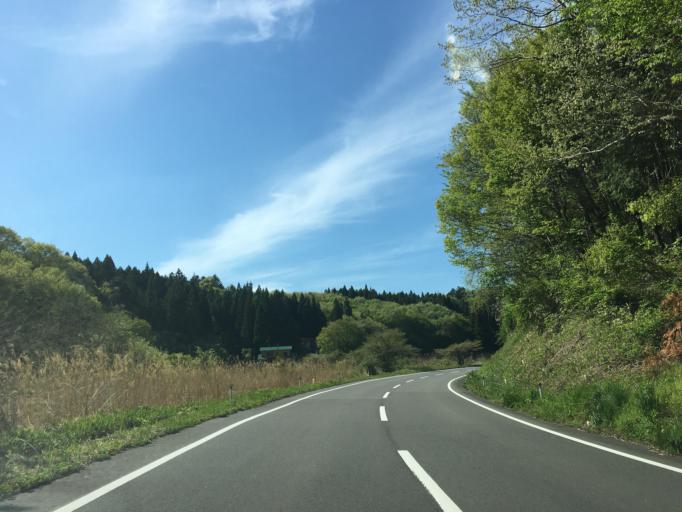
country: JP
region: Fukushima
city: Funehikimachi-funehiki
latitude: 37.3210
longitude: 140.6208
